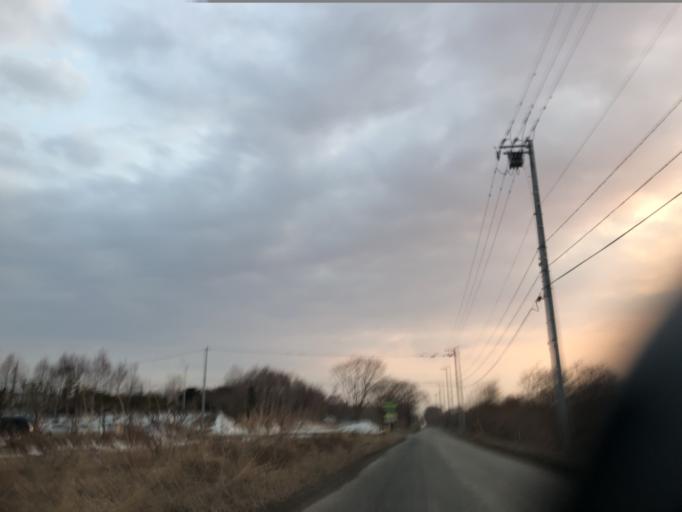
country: JP
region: Hokkaido
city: Chitose
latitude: 42.8578
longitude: 141.7082
